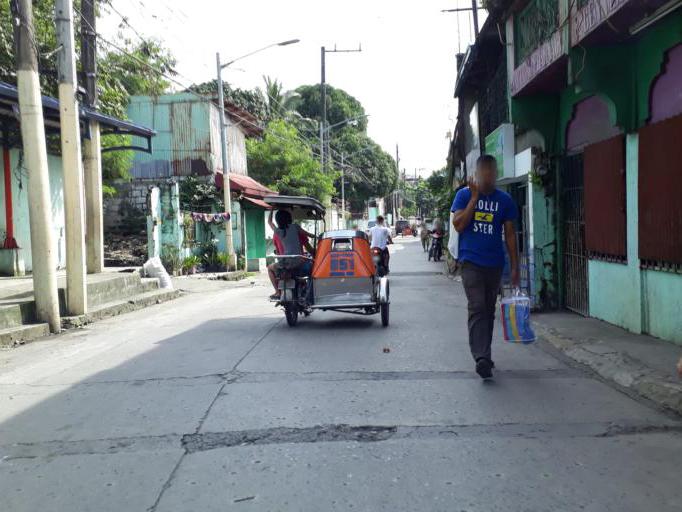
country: PH
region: Calabarzon
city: Bagong Pagasa
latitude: 14.6735
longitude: 121.0021
